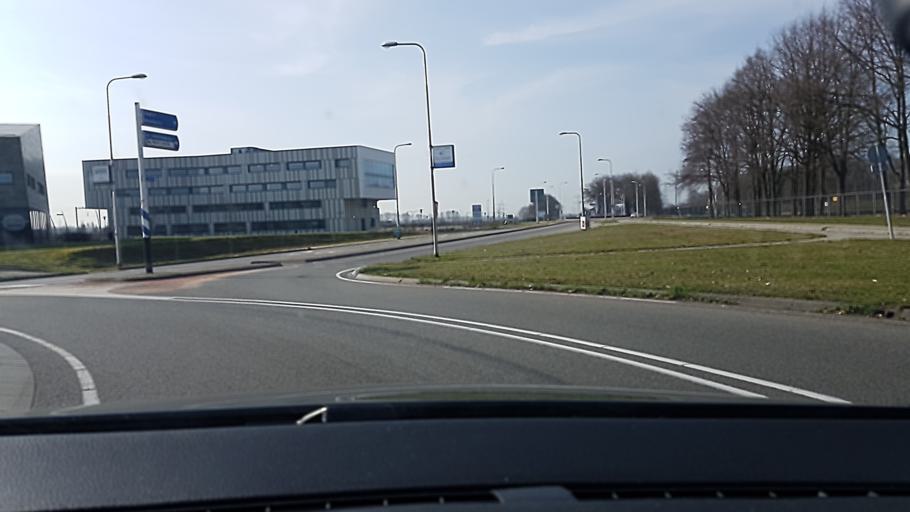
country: NL
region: Limburg
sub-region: Gemeente Roermond
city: Roermond
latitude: 51.1659
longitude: 5.9626
